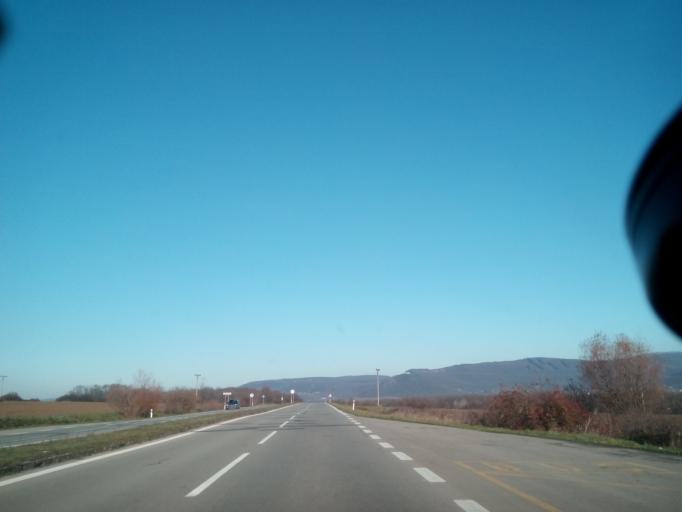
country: SK
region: Kosicky
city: Vinne
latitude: 48.7789
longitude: 21.9472
